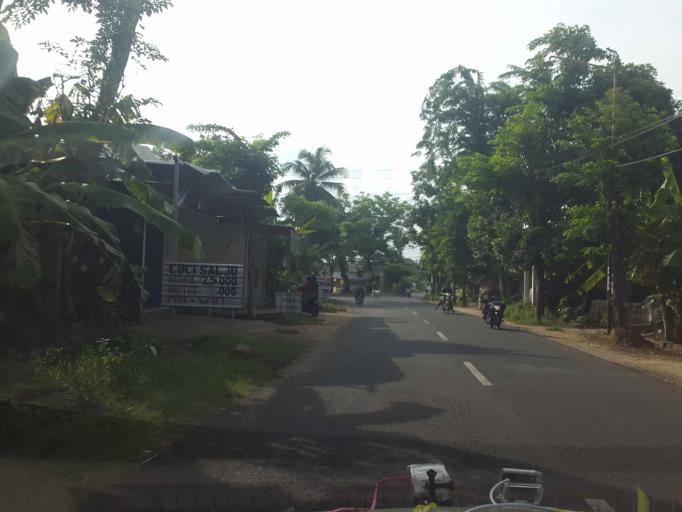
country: ID
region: East Java
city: Bereklorong
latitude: -7.0364
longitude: 113.9080
